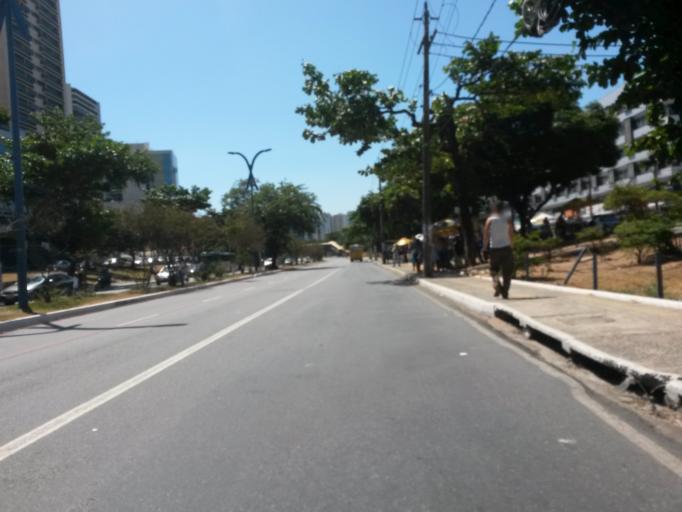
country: BR
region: Bahia
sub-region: Salvador
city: Salvador
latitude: -12.9969
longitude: -38.4643
